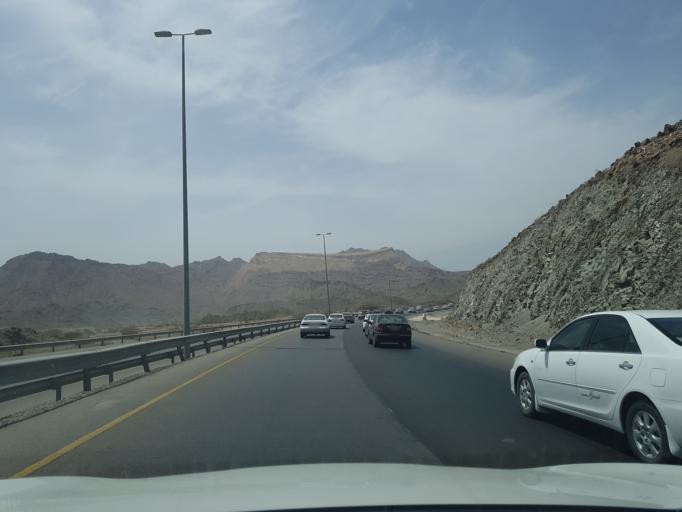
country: OM
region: Muhafazat ad Dakhiliyah
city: Bidbid
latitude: 23.4709
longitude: 58.1959
